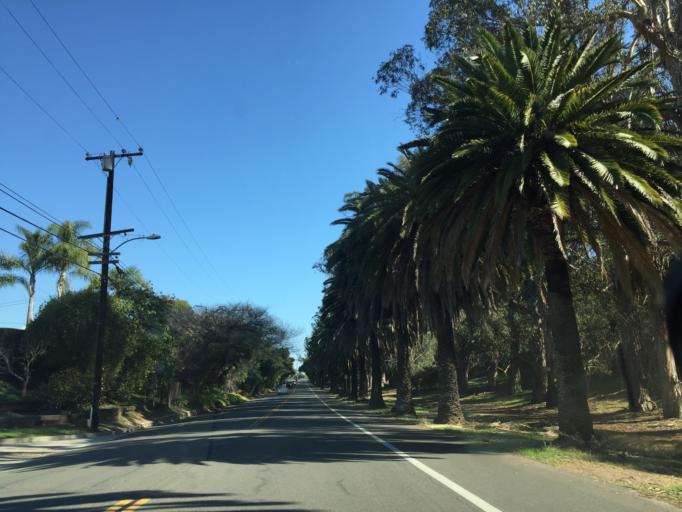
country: US
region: California
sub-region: Santa Barbara County
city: Mission Canyon
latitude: 34.4370
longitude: -119.7598
